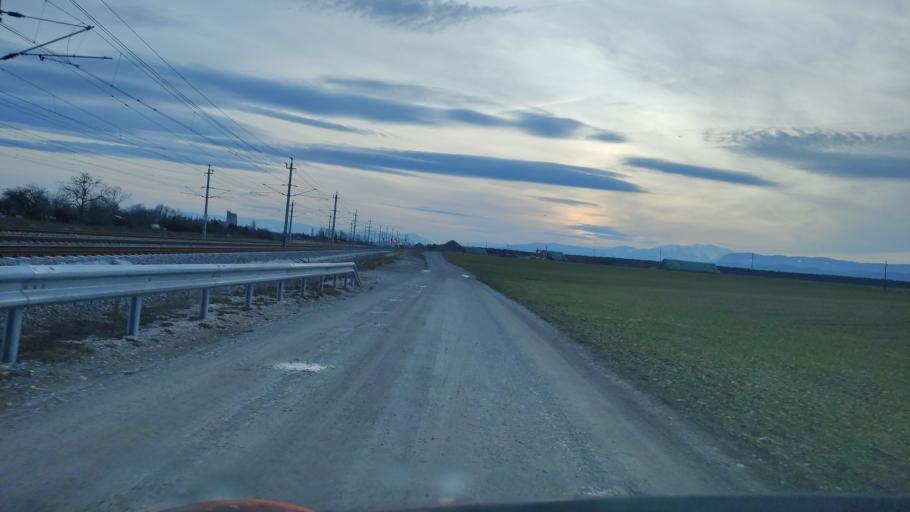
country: AT
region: Lower Austria
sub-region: Politischer Bezirk Wiener Neustadt
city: Lichtenworth
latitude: 47.8494
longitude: 16.2957
